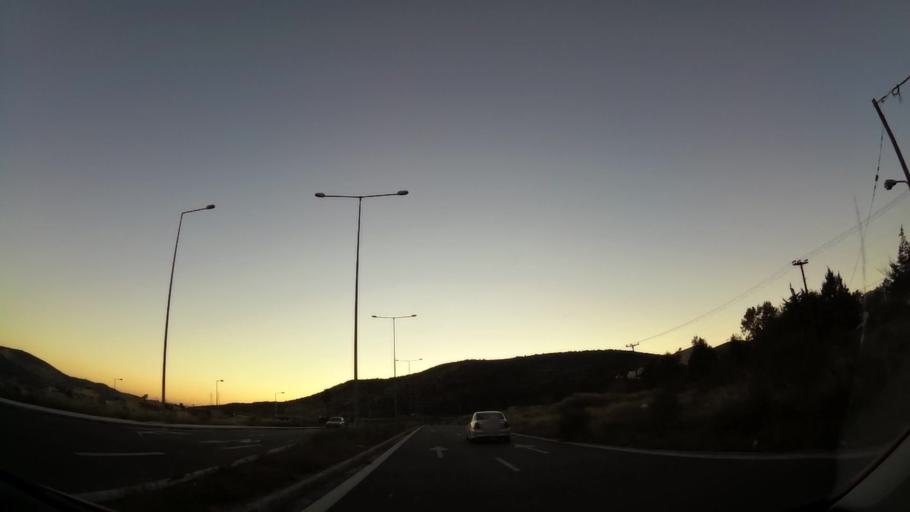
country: GR
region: Attica
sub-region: Nomarchia Dytikis Attikis
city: Ano Liosia
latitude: 38.0955
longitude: 23.6910
